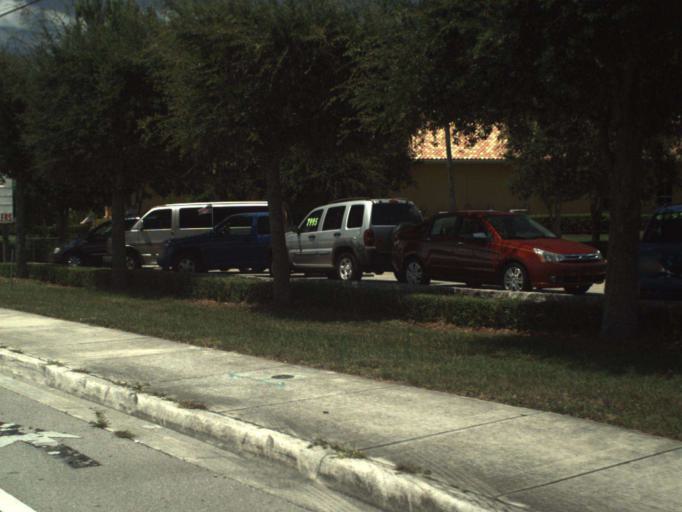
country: US
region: Florida
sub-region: Saint Lucie County
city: River Park
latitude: 27.3239
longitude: -80.3191
